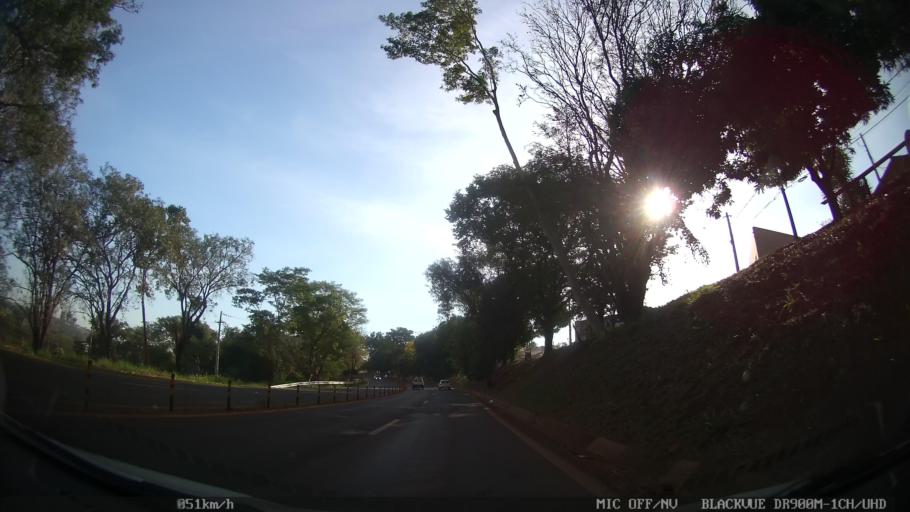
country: BR
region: Sao Paulo
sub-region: Ribeirao Preto
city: Ribeirao Preto
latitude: -21.2626
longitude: -47.8188
